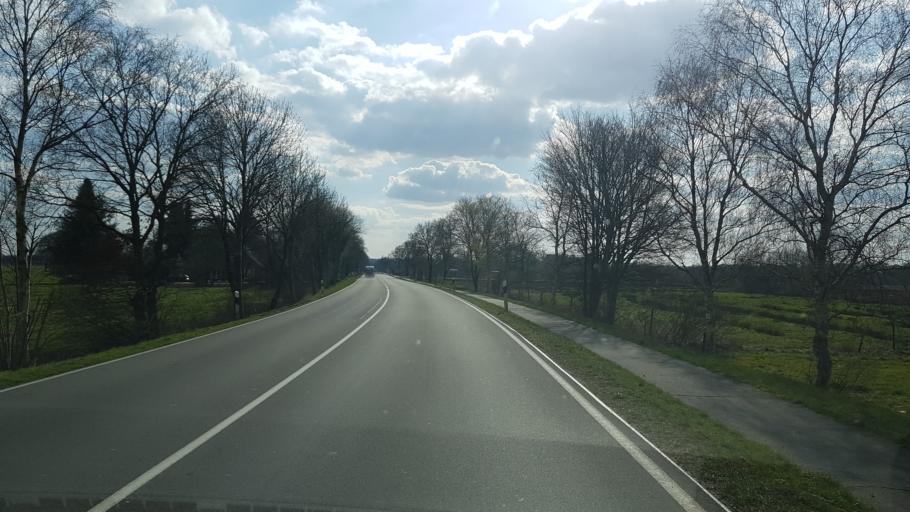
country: DE
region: Lower Saxony
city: Rastede
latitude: 53.2467
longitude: 8.2946
